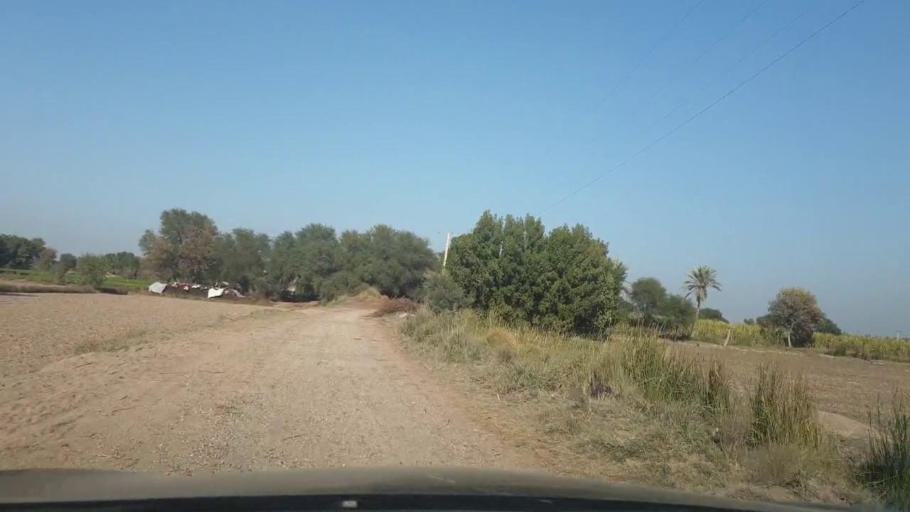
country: PK
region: Sindh
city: Mirpur Mathelo
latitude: 28.1415
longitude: 69.5969
